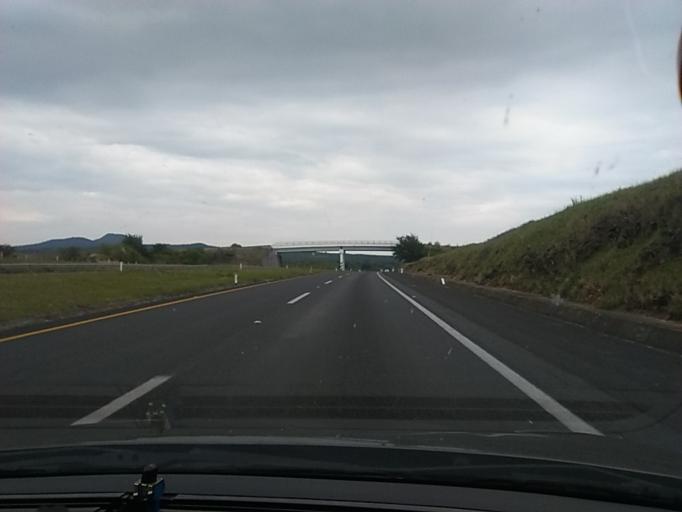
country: MX
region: Michoacan
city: Penjamillo de Degollado
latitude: 20.0290
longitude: -101.9195
